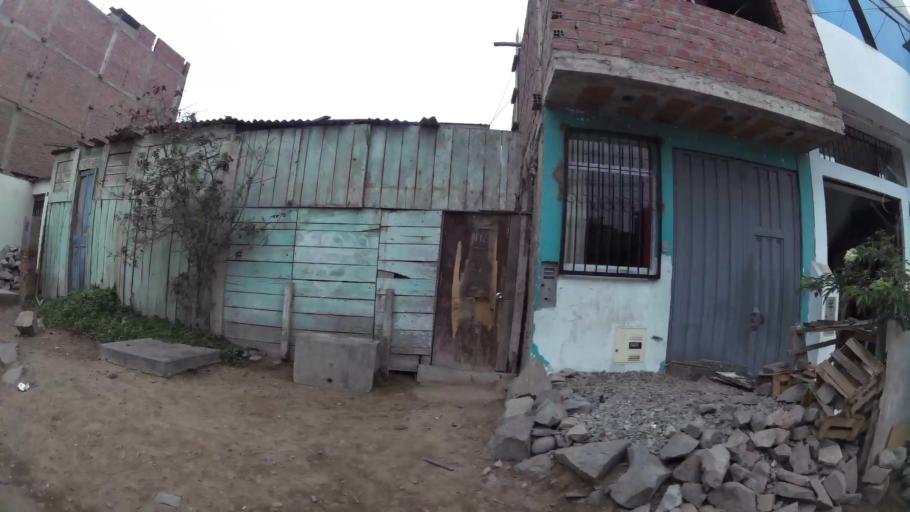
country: PE
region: Lima
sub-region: Lima
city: Surco
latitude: -12.1795
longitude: -76.9608
